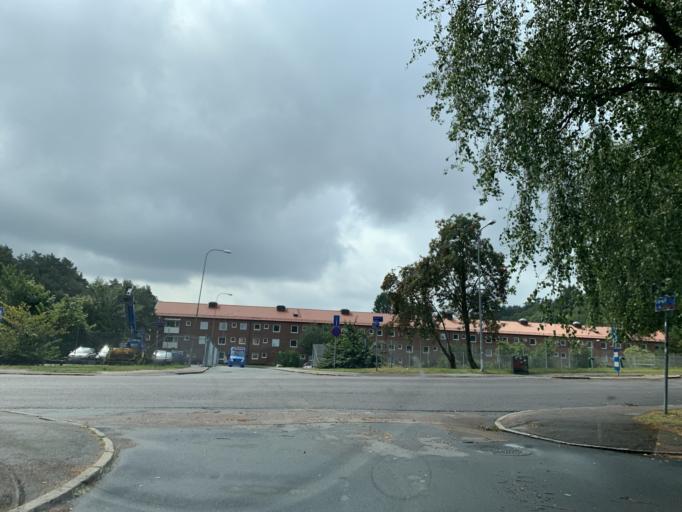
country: SE
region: Vaestra Goetaland
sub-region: Goteborg
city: Eriksbo
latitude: 57.7475
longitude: 12.0294
